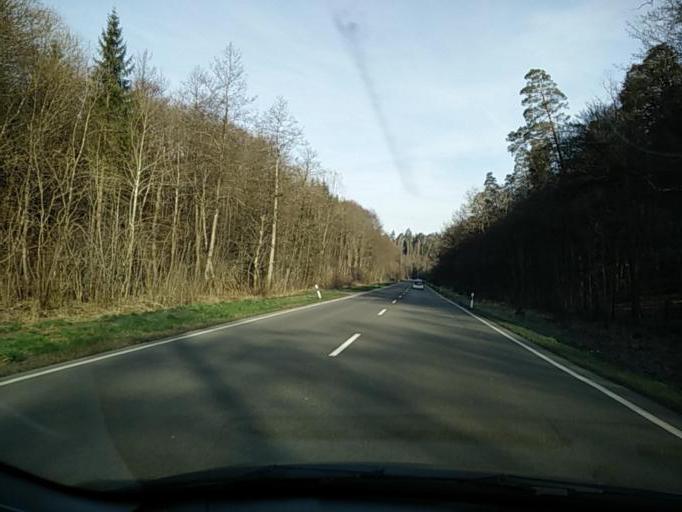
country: DE
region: Baden-Wuerttemberg
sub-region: Tuebingen Region
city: Dettenhausen
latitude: 48.5706
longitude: 9.0737
